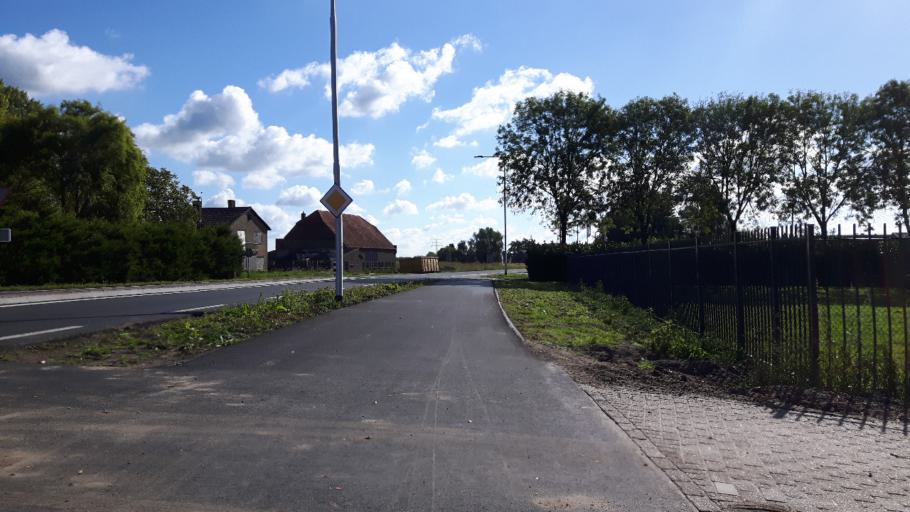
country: NL
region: Gelderland
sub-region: Gemeente Culemborg
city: Culemborg
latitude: 51.9447
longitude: 5.2422
